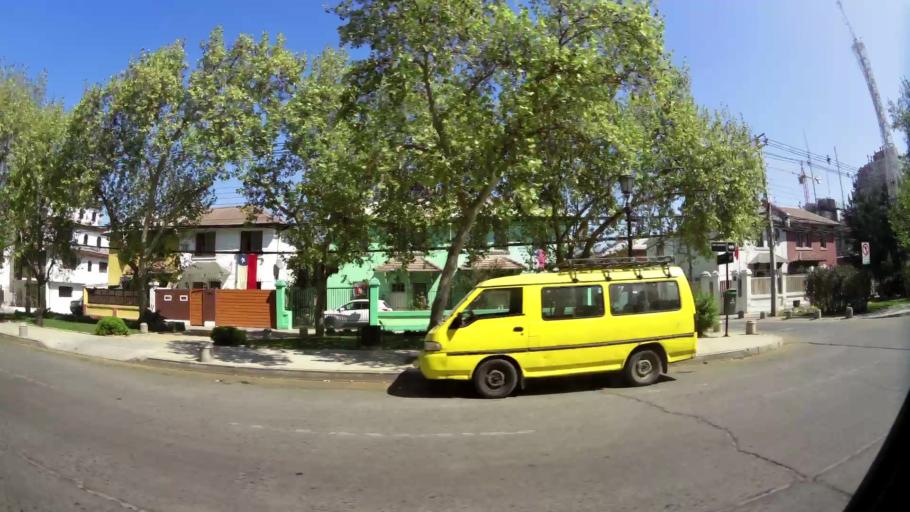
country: CL
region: Santiago Metropolitan
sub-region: Provincia de Santiago
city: Santiago
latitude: -33.4693
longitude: -70.6635
